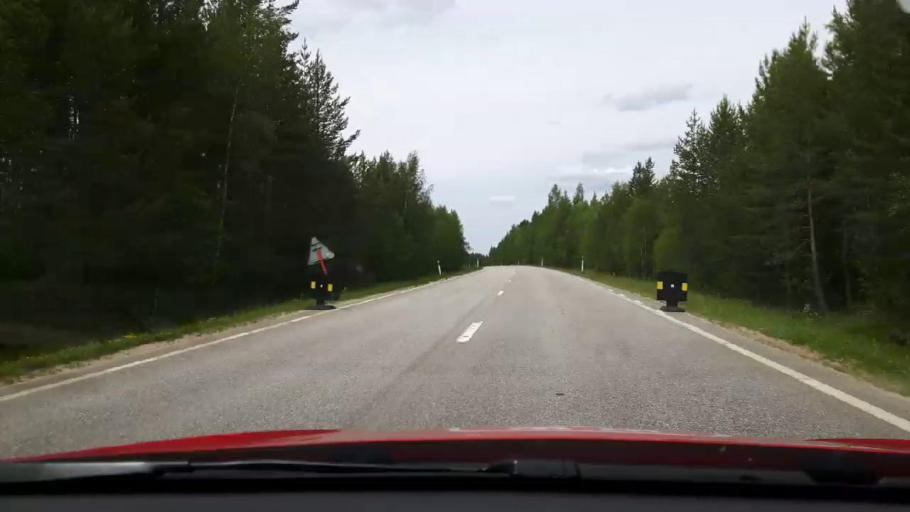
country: SE
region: Jaemtland
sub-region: Harjedalens Kommun
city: Sveg
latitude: 62.0772
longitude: 14.2654
